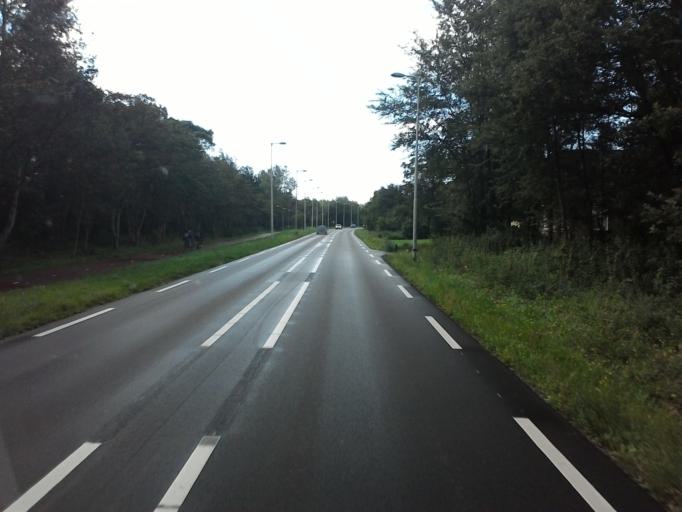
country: NL
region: North Holland
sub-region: Gemeente Beverwijk
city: Beverwijk
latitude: 52.4885
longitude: 4.6205
